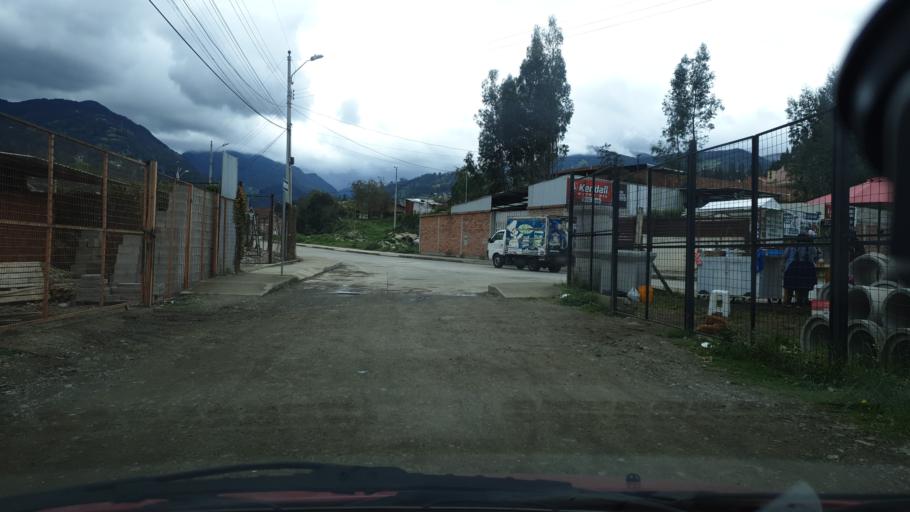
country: EC
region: Azuay
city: Cuenca
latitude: -2.8818
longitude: -79.0576
